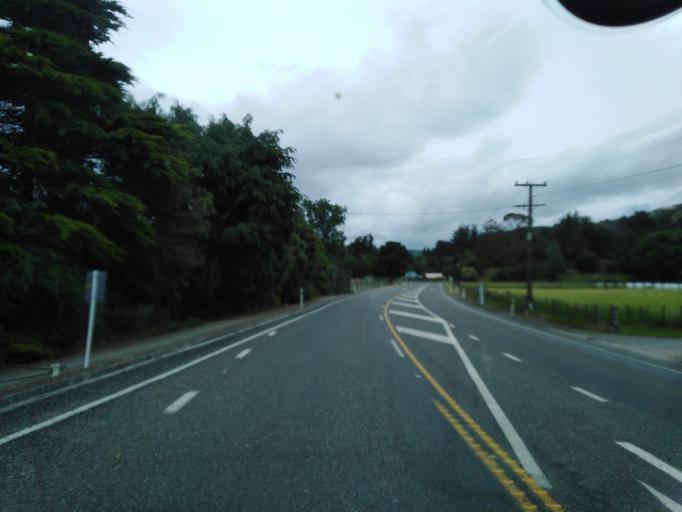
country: NZ
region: Tasman
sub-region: Tasman District
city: Wakefield
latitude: -41.4547
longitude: 172.9564
